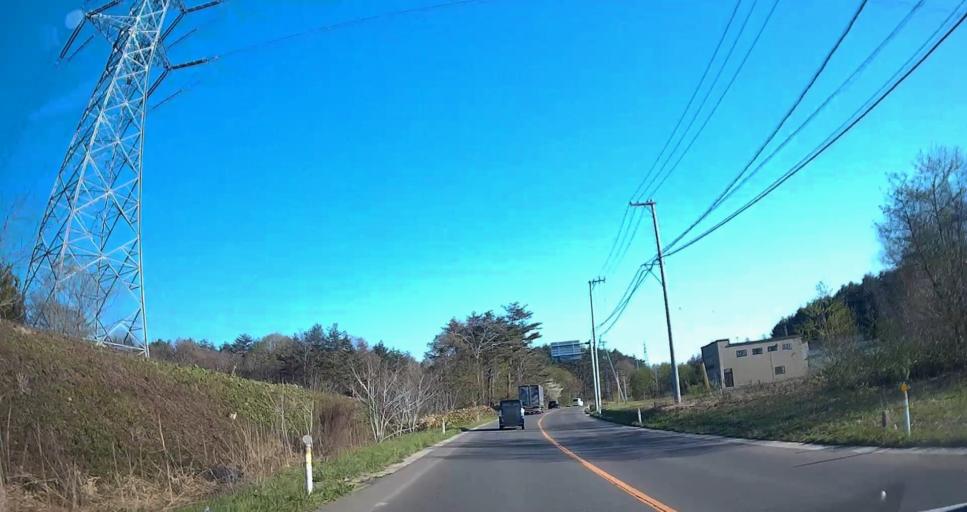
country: JP
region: Aomori
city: Mutsu
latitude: 41.3431
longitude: 141.2150
